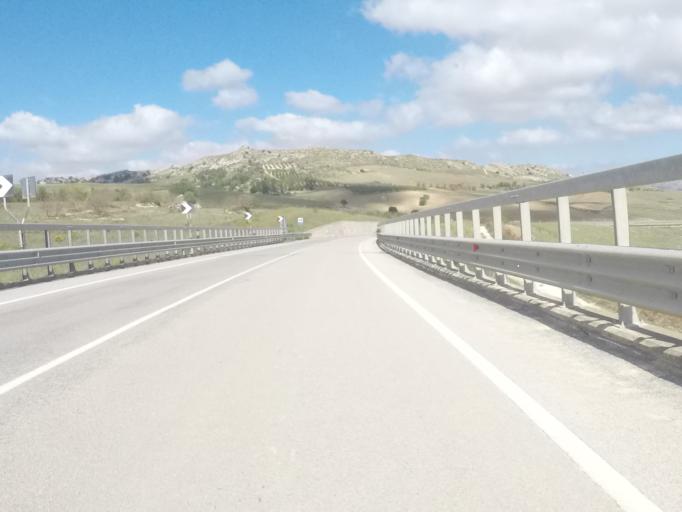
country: IT
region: Sicily
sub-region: Enna
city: Pietraperzia
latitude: 37.4169
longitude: 14.1199
